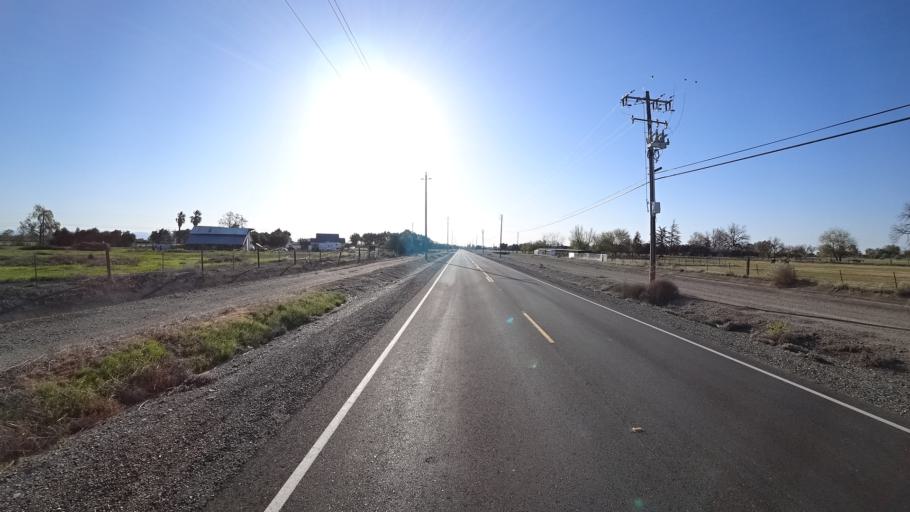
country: US
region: California
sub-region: Glenn County
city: Orland
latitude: 39.7675
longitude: -122.2496
